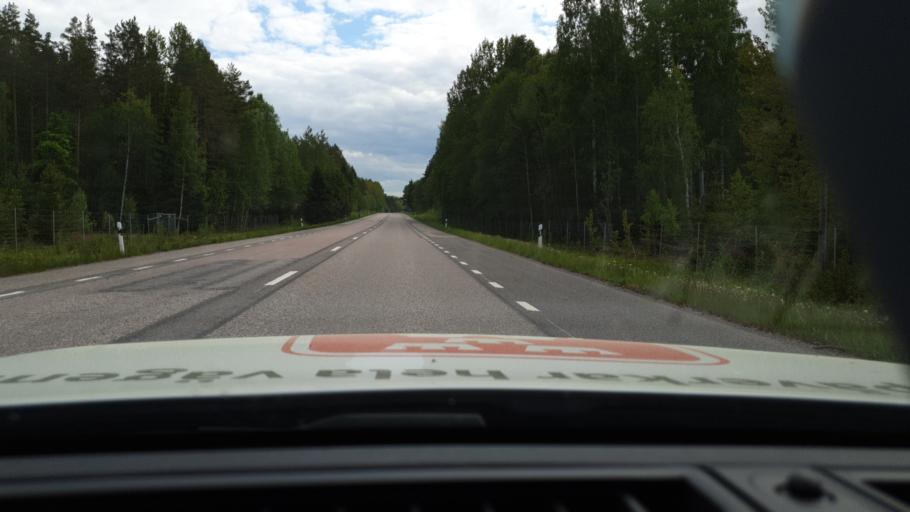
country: SE
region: Uppsala
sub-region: Alvkarleby Kommun
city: AElvkarleby
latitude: 60.5929
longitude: 17.4629
